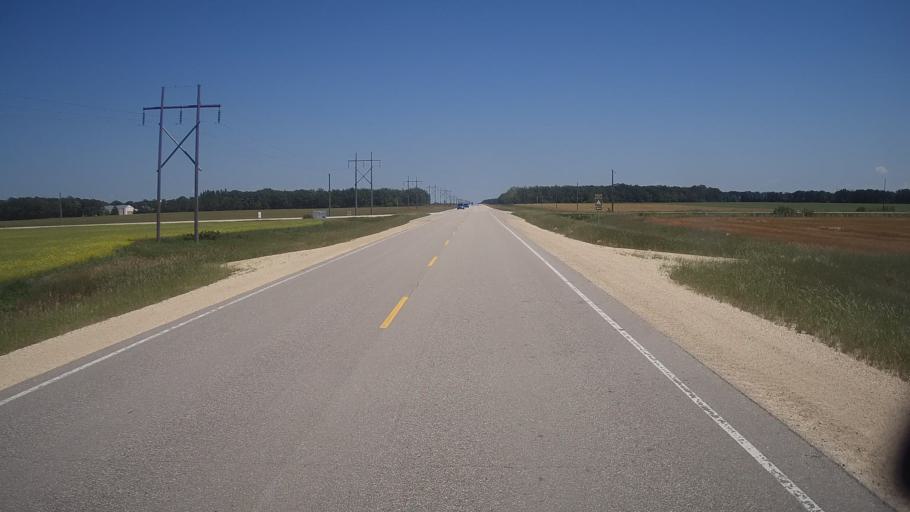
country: CA
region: Manitoba
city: Stonewall
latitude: 50.1227
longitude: -97.4846
